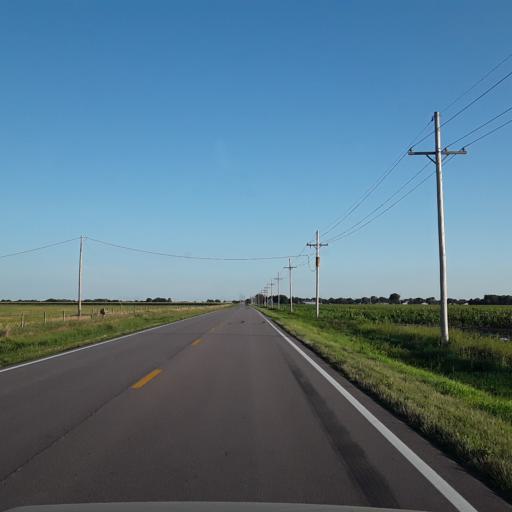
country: US
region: Nebraska
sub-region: Hall County
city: Grand Island
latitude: 40.9561
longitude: -98.3207
